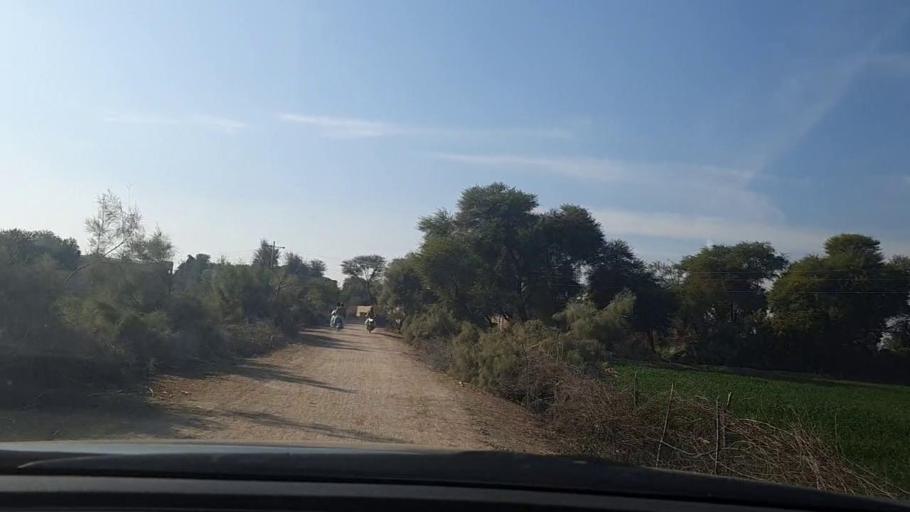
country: PK
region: Sindh
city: Sehwan
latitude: 26.2998
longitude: 67.9876
